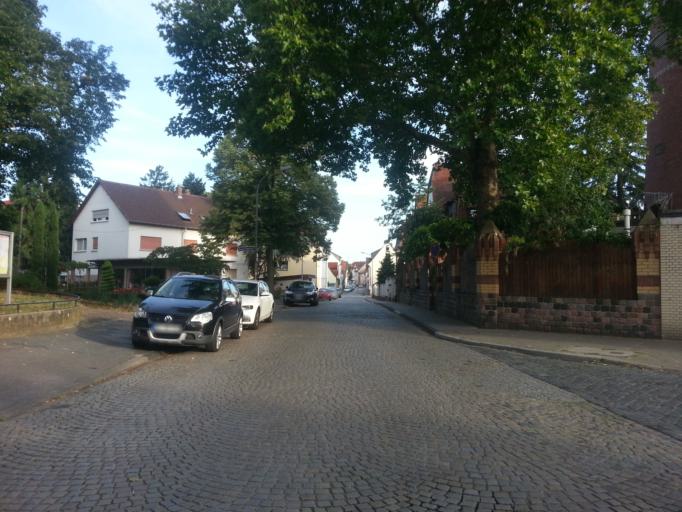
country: DE
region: Baden-Wuerttemberg
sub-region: Karlsruhe Region
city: Ilvesheim
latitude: 49.4906
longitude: 8.5291
